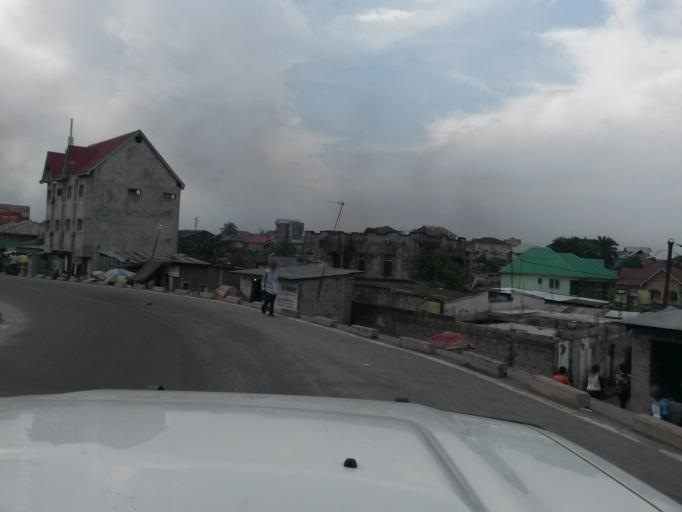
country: CD
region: Kinshasa
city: Masina
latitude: -4.3809
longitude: 15.3509
